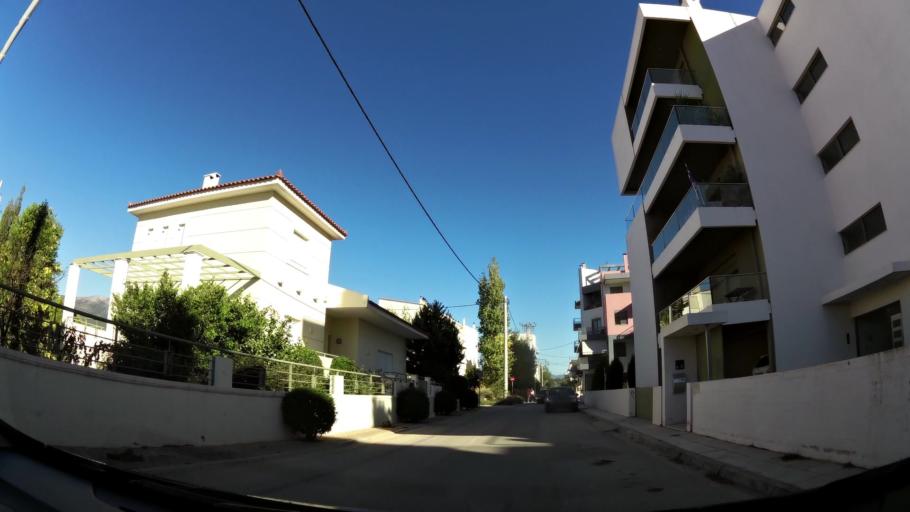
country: GR
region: Attica
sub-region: Nomarchia Anatolikis Attikis
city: Koropi
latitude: 37.9058
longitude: 23.8694
